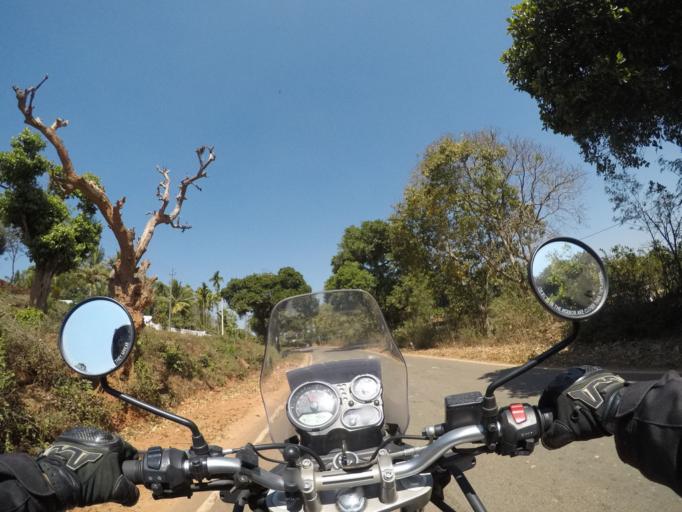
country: IN
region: Karnataka
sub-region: Chikmagalur
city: Mudigere
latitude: 13.0305
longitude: 75.6957
